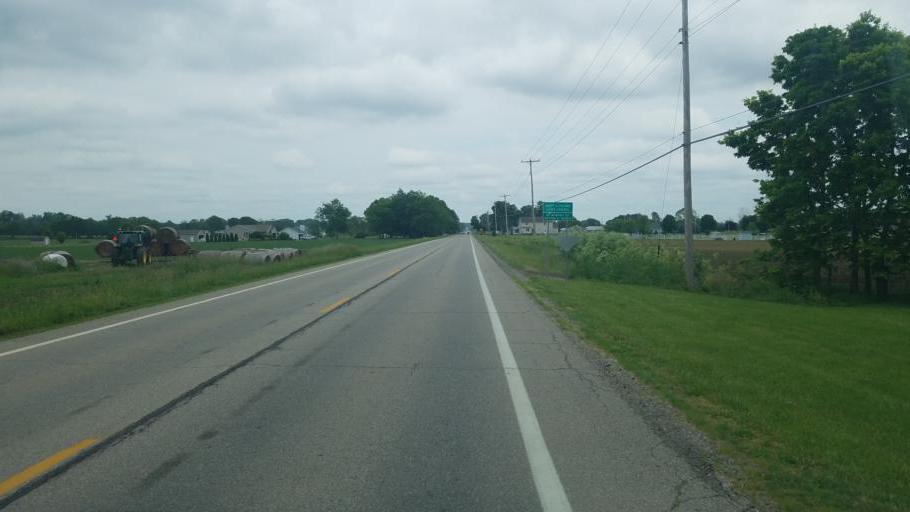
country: US
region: Ohio
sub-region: Fairfield County
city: Millersport
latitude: 39.9586
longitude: -82.5745
